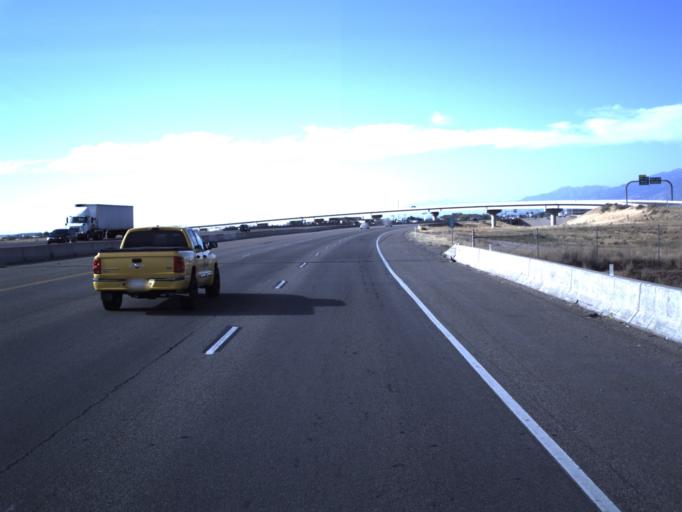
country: US
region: Utah
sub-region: Salt Lake County
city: Salt Lake City
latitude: 40.7600
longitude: -111.9507
